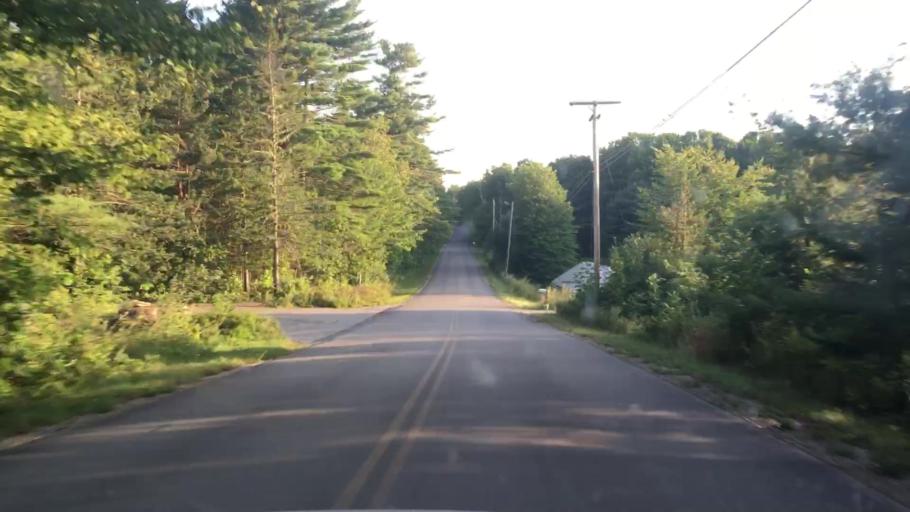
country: US
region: Maine
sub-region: Penobscot County
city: Hampden
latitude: 44.7097
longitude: -68.8877
